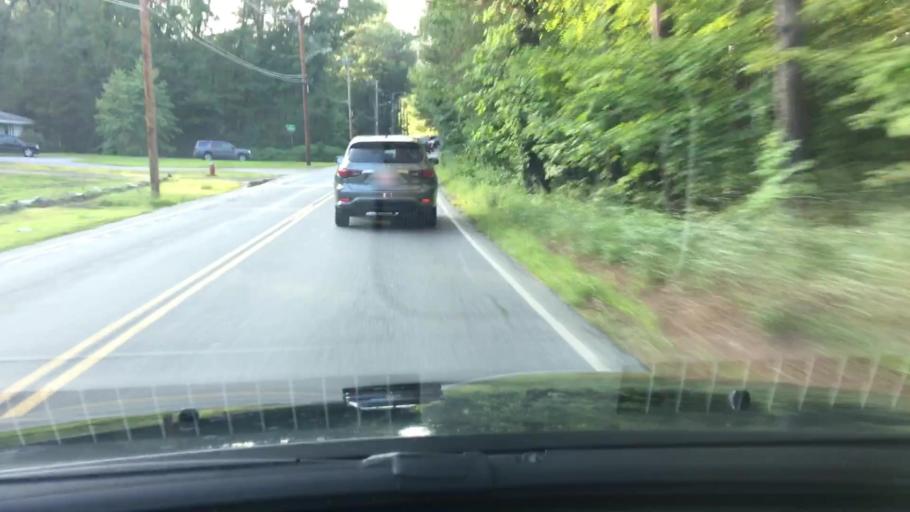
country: US
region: Massachusetts
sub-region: Worcester County
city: West Boylston
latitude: 42.3541
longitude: -71.7663
